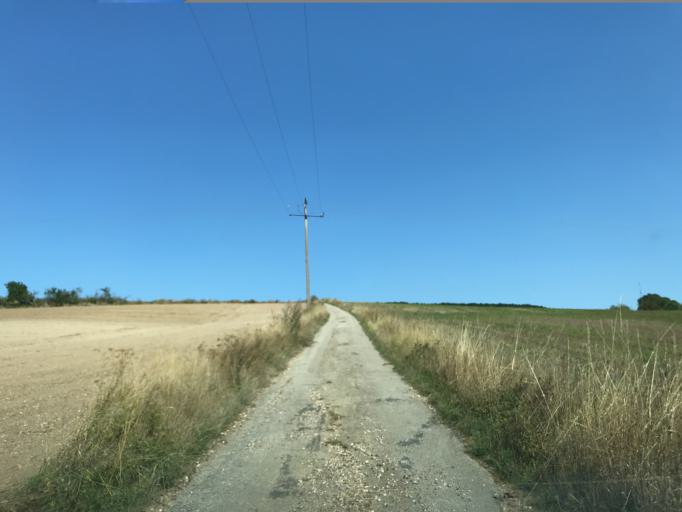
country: FR
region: Haute-Normandie
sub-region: Departement de l'Eure
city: Heudreville-sur-Eure
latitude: 49.1245
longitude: 1.2244
